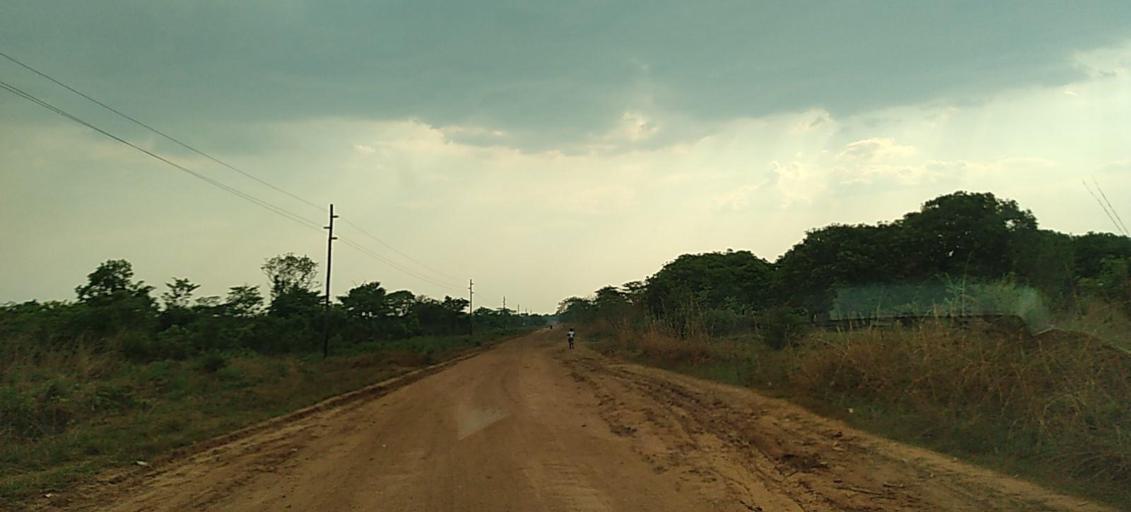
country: ZM
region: Copperbelt
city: Kalulushi
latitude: -12.9487
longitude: 27.9126
